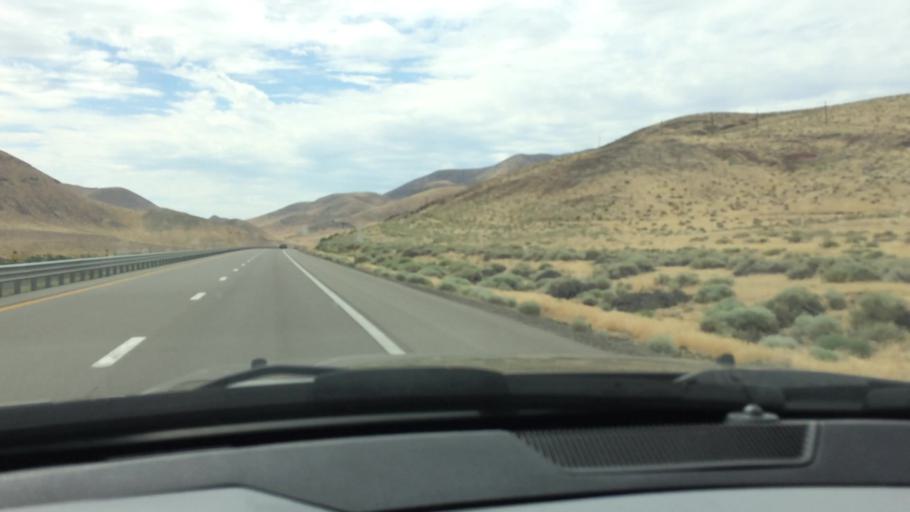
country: US
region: Nevada
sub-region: Lyon County
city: Fernley
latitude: 39.5893
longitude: -119.4386
